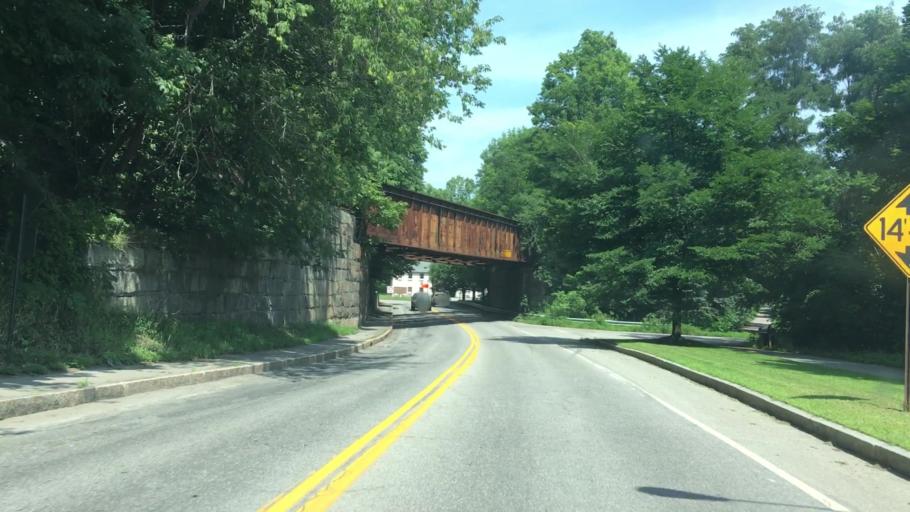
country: US
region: Maine
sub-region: Kennebec County
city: Hallowell
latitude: 44.2888
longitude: -69.7894
